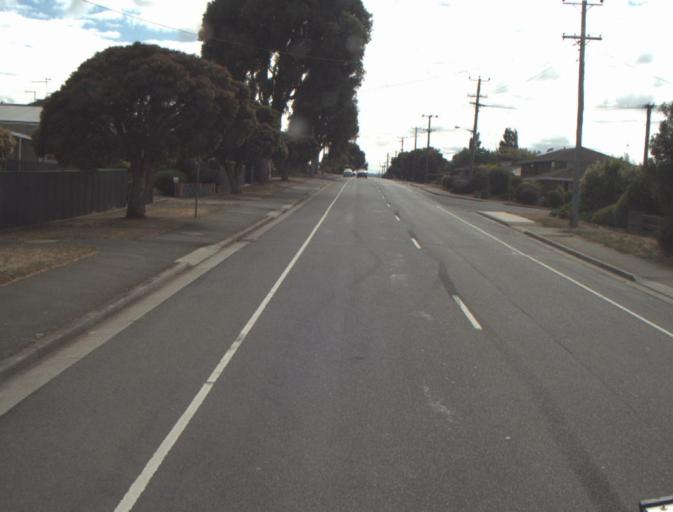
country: AU
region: Tasmania
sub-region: Launceston
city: Summerhill
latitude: -41.4657
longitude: 147.1325
